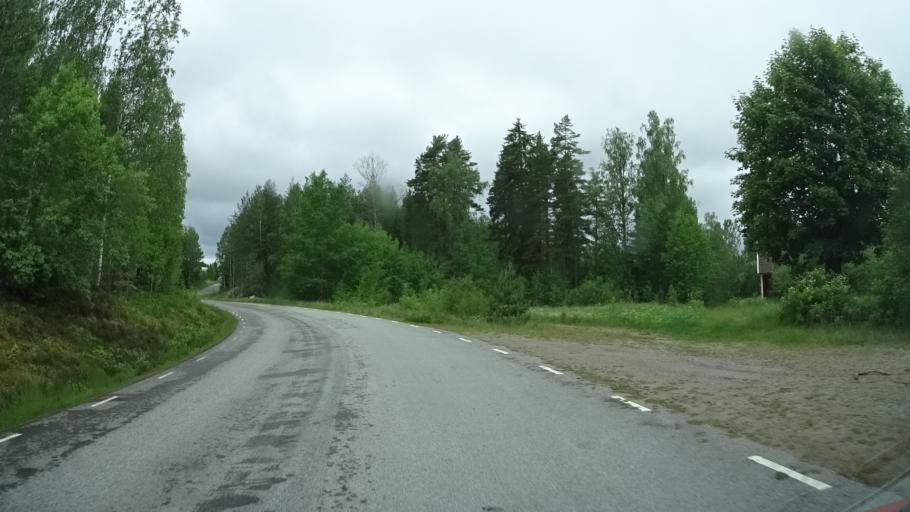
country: SE
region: Joenkoeping
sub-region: Eksjo Kommun
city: Mariannelund
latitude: 57.7017
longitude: 15.6472
